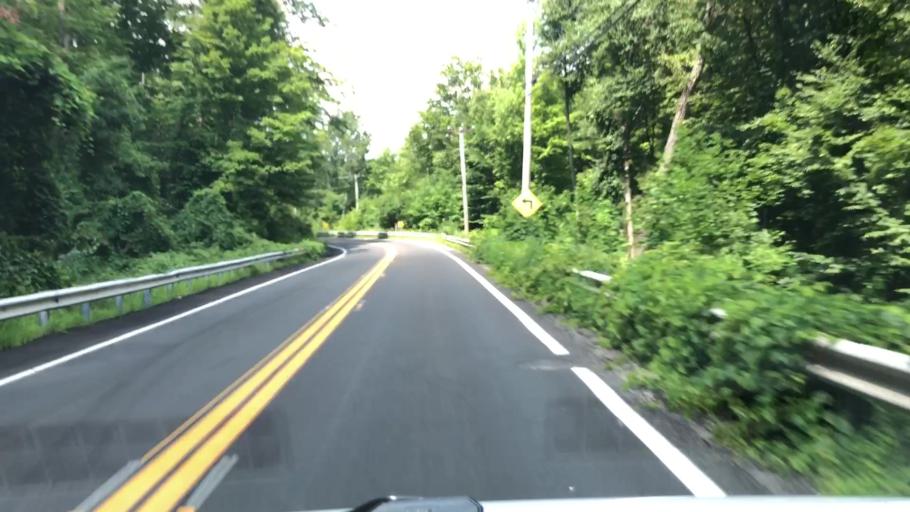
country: US
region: Massachusetts
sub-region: Franklin County
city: Ashfield
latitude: 42.5251
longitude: -72.7837
